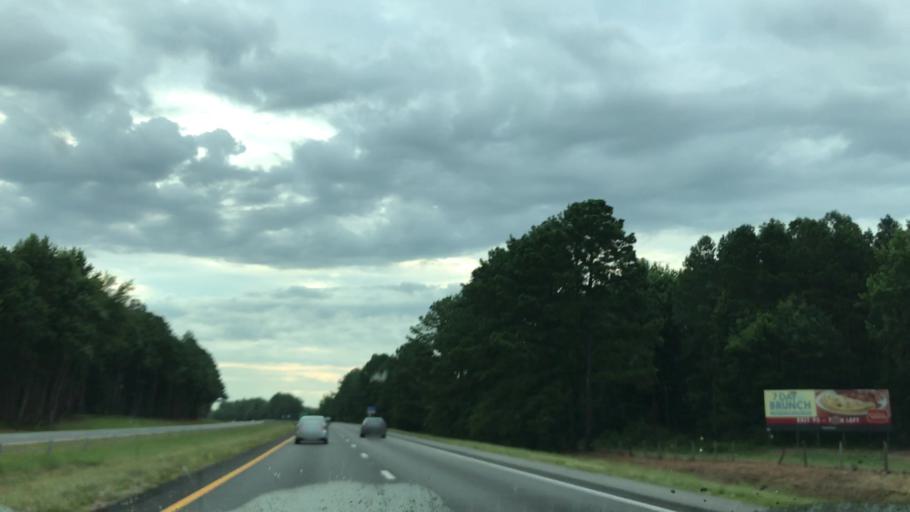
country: US
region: North Carolina
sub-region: Johnston County
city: Four Oaks
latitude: 35.4249
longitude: -78.4424
